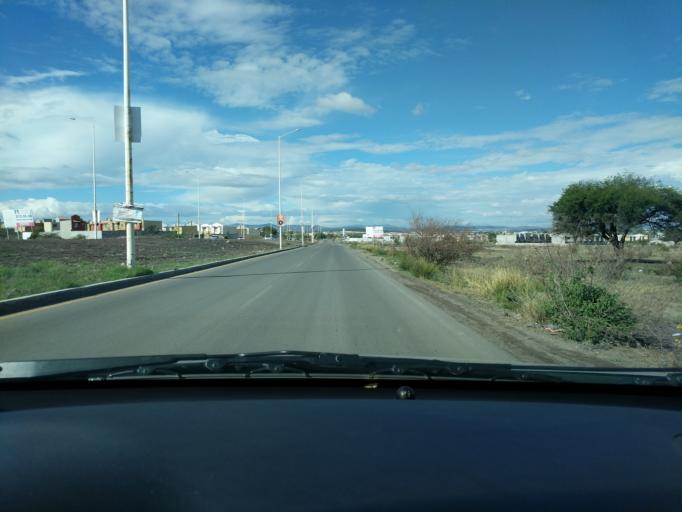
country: MX
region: Queretaro
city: El Colorado
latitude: 20.5872
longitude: -100.2836
